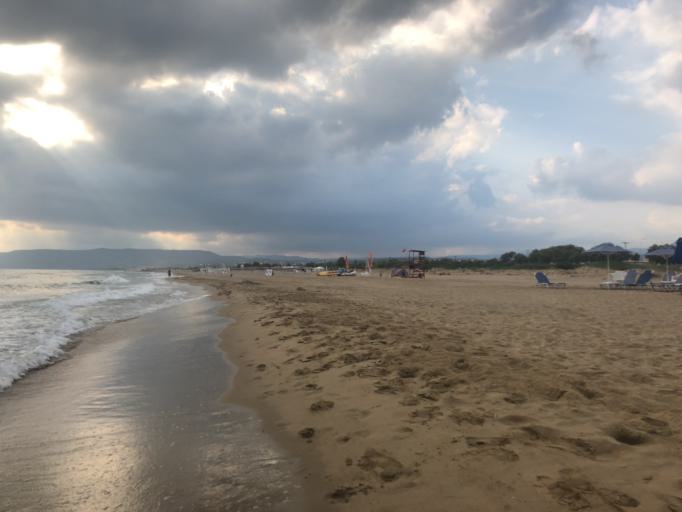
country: GR
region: Crete
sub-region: Nomos Chanias
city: Georgioupolis
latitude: 35.3566
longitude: 24.2792
